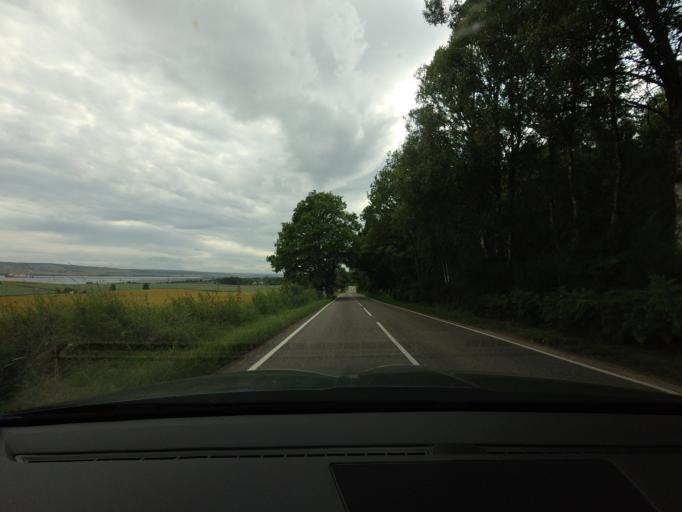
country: GB
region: Scotland
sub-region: Highland
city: Alness
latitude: 57.6965
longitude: -4.2891
